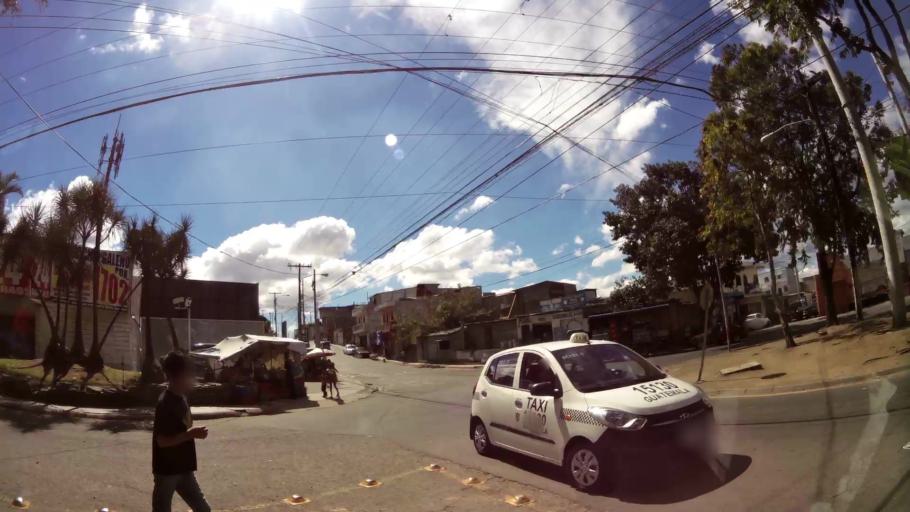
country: GT
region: Guatemala
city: Villa Nueva
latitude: 14.5462
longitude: -90.5526
